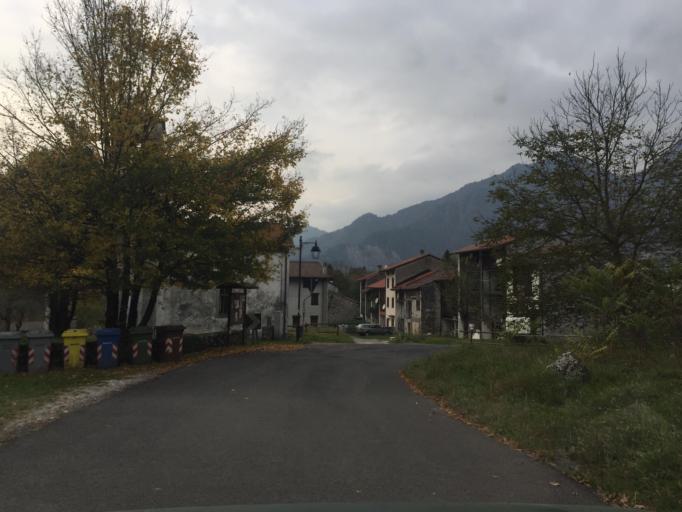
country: IT
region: Friuli Venezia Giulia
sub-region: Provincia di Pordenone
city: Andreis
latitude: 46.1961
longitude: 12.6310
